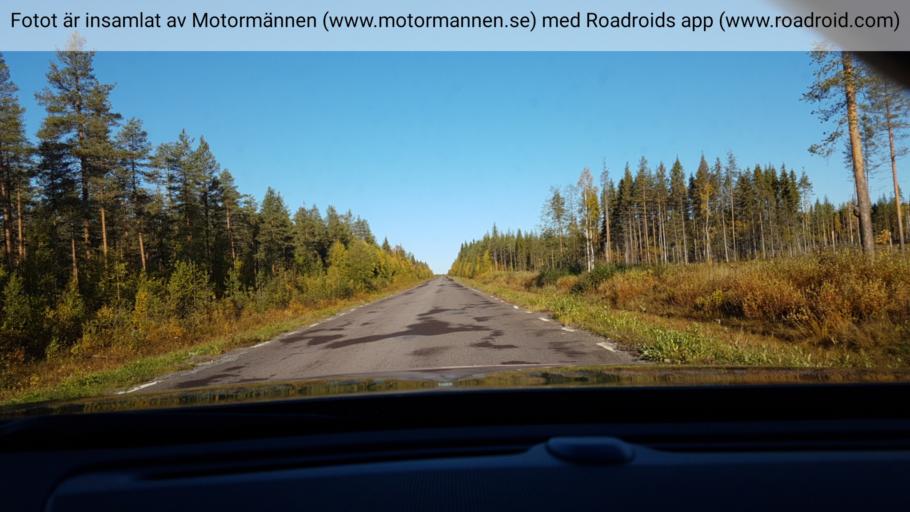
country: SE
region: Norrbotten
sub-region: Bodens Kommun
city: Boden
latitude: 66.0139
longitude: 21.5263
